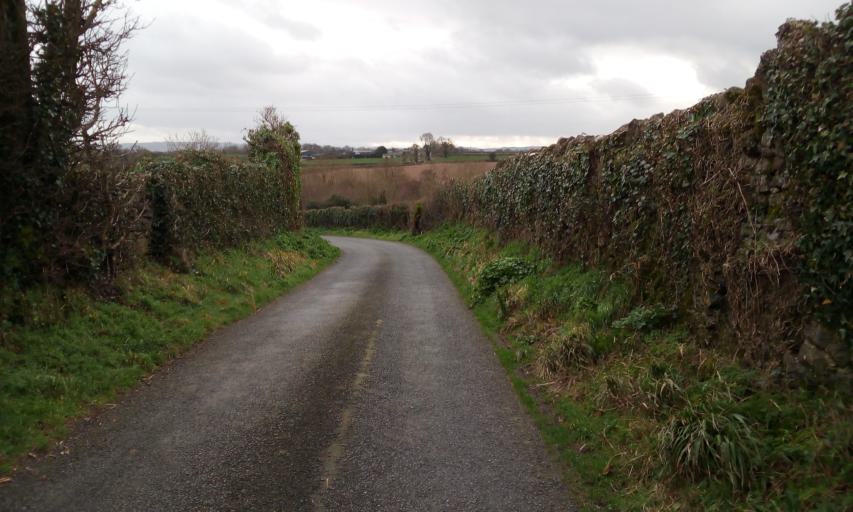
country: IE
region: Leinster
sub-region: Kilkenny
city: Callan
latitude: 52.5439
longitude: -7.3160
